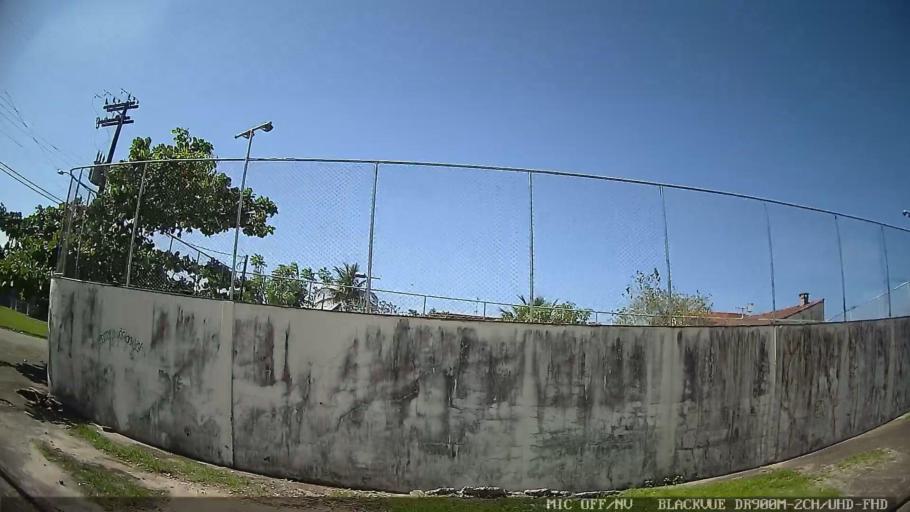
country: BR
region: Sao Paulo
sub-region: Peruibe
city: Peruibe
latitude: -24.3148
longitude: -46.9944
